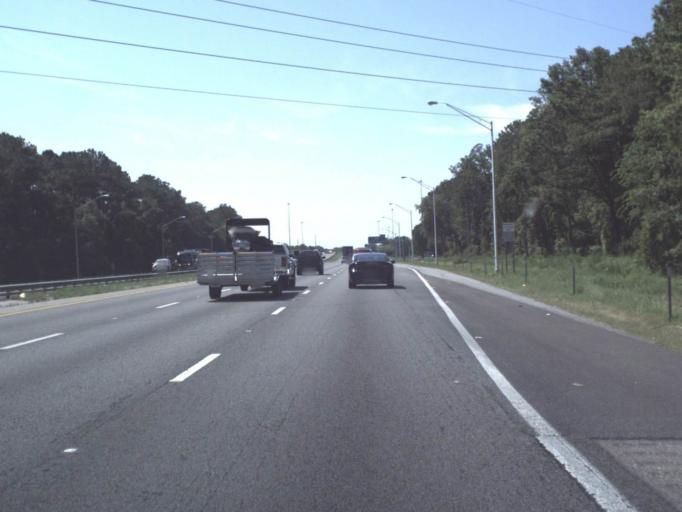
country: US
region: Florida
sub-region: Clay County
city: Bellair-Meadowbrook Terrace
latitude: 30.2768
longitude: -81.7701
